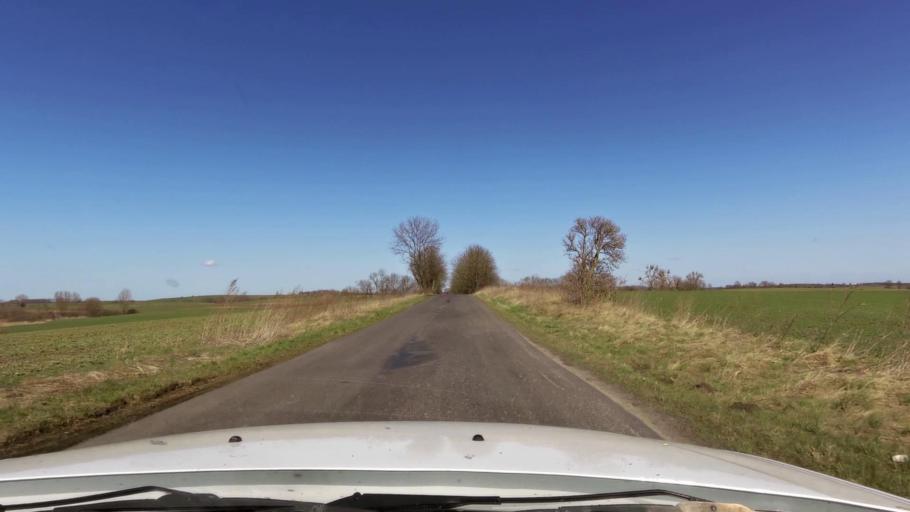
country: PL
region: West Pomeranian Voivodeship
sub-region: Powiat gryfinski
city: Cedynia
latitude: 52.8739
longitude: 14.2866
